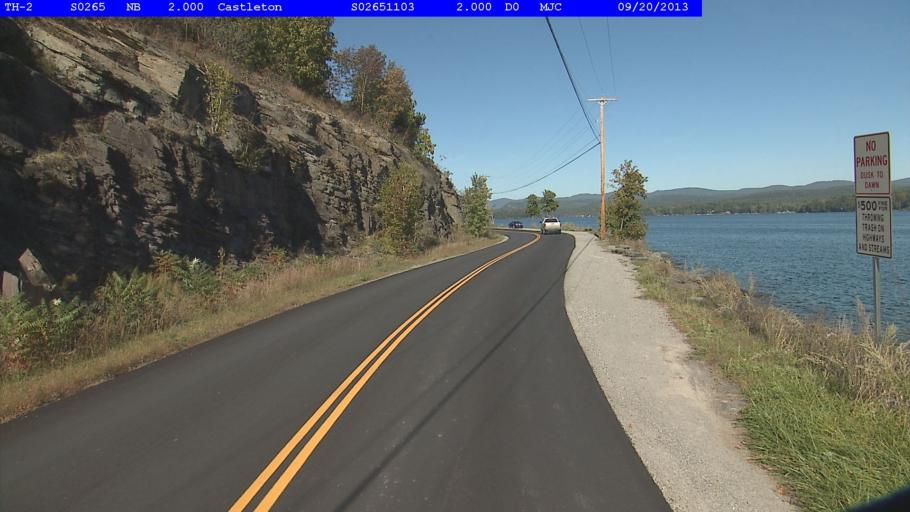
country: US
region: Vermont
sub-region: Rutland County
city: Fair Haven
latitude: 43.6311
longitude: -73.2330
